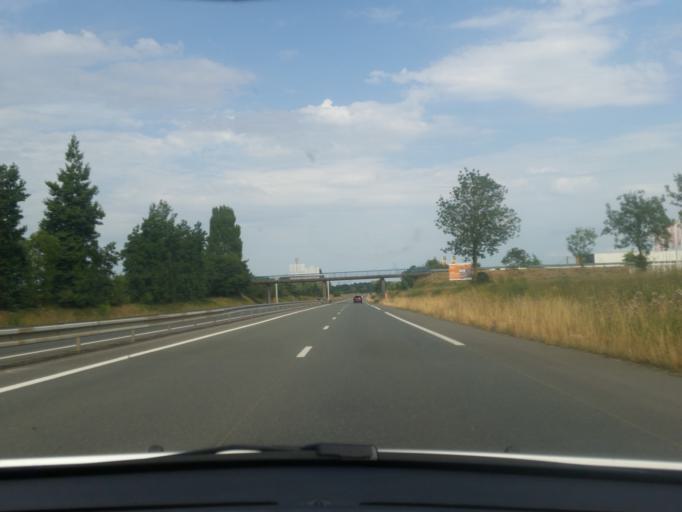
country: FR
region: Pays de la Loire
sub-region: Departement de Maine-et-Loire
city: Saint-Lambert-la-Potherie
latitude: 47.4655
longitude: -0.6667
